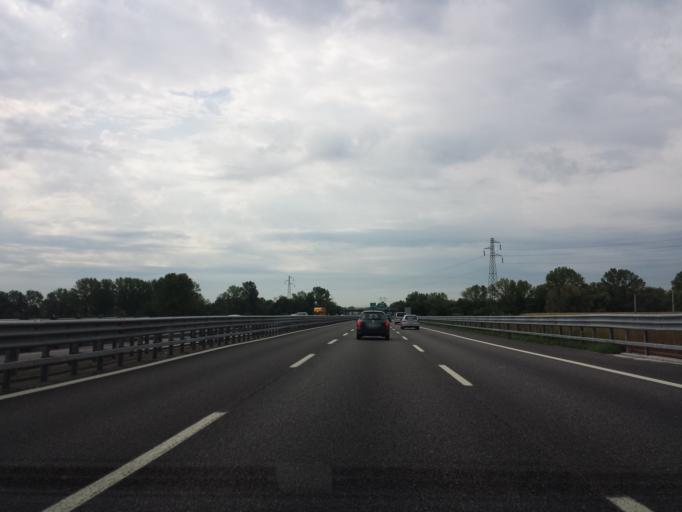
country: IT
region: Lombardy
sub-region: Citta metropolitana di Milano
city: Cesano Boscone
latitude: 45.4405
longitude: 9.0737
